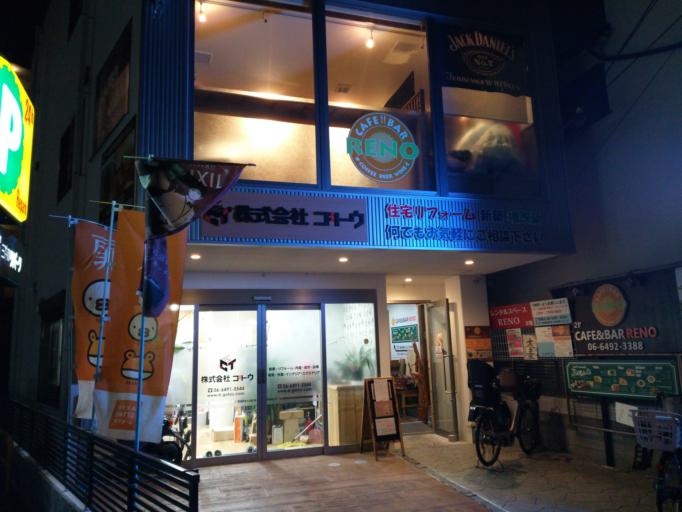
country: JP
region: Osaka
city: Toyonaka
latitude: 34.7514
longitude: 135.4494
